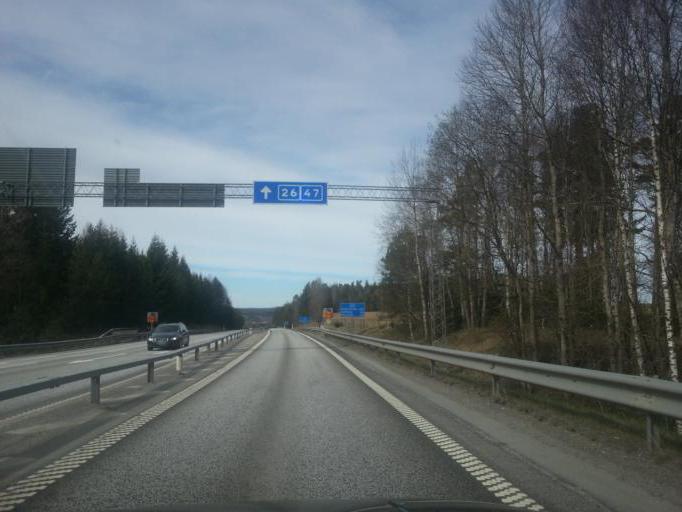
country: SE
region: Joenkoeping
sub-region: Jonkopings Kommun
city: Jonkoping
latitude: 57.7924
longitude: 14.1008
